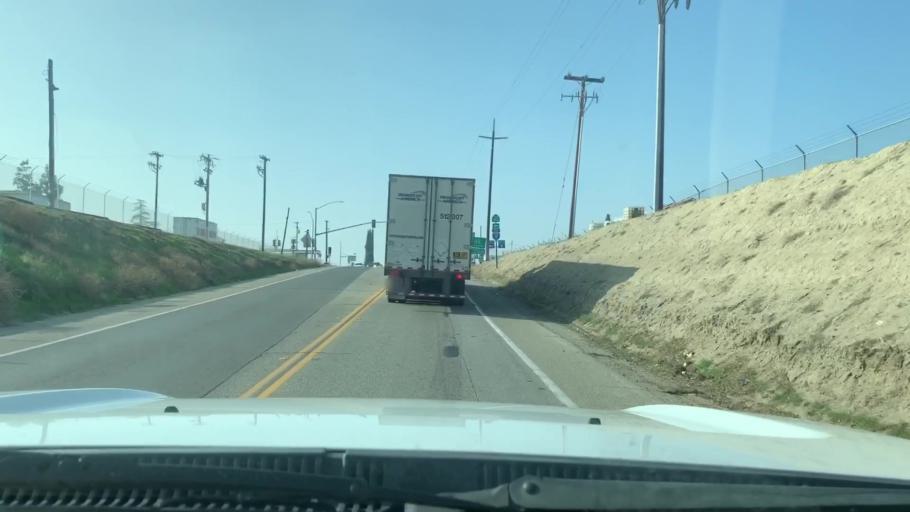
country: US
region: California
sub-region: Kern County
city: Wasco
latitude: 35.6016
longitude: -119.3322
